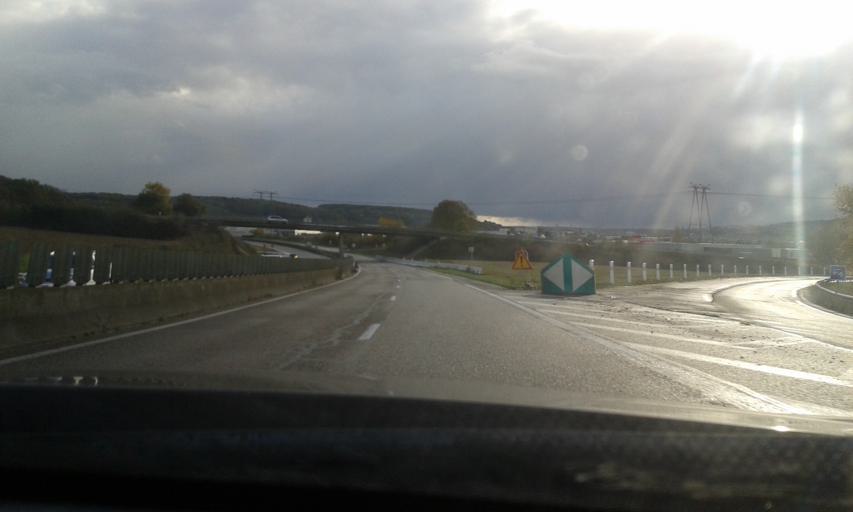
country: FR
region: Haute-Normandie
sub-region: Departement de l'Eure
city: Gravigny
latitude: 49.0613
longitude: 1.1748
